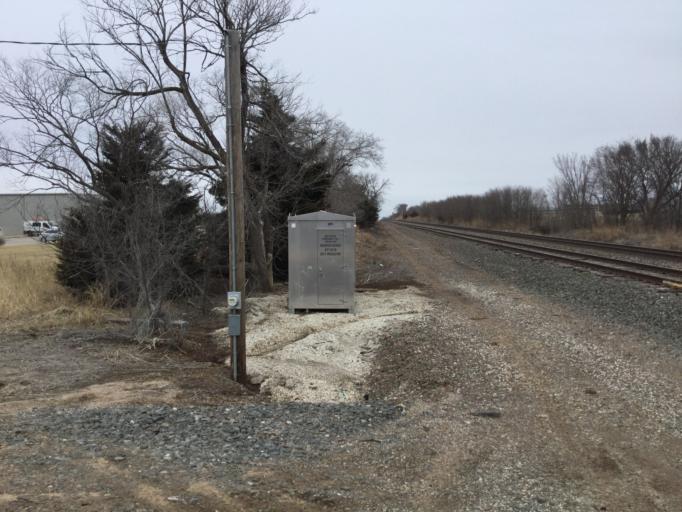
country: US
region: Kansas
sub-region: Sedgwick County
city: Derby
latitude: 37.5481
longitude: -97.2728
